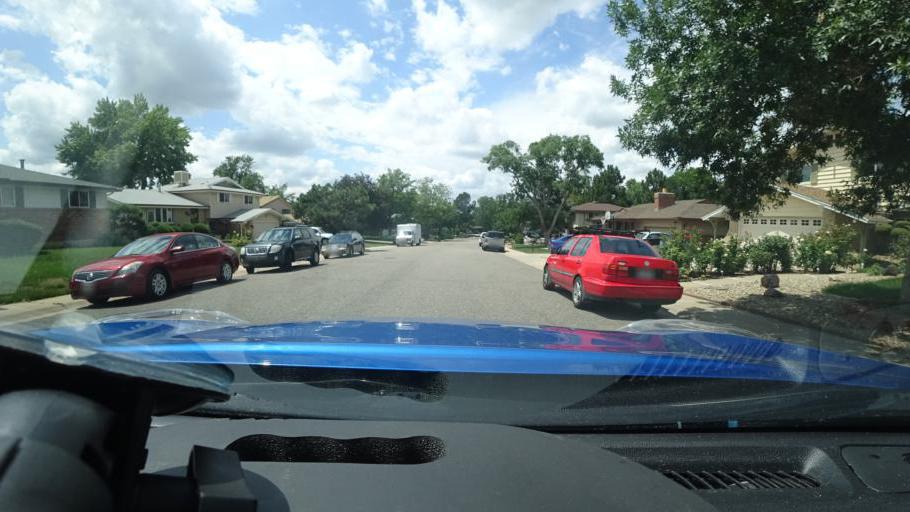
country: US
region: Colorado
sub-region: Adams County
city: Aurora
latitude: 39.7003
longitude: -104.8362
